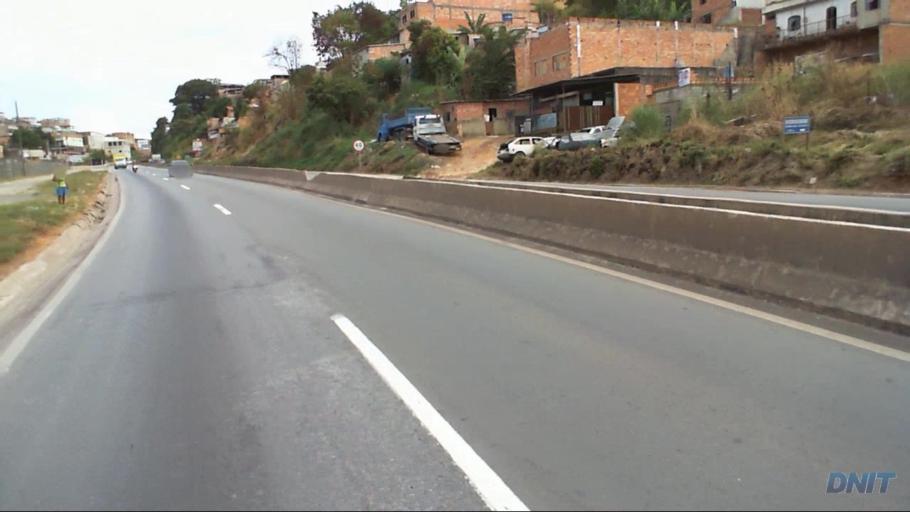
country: BR
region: Minas Gerais
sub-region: Santa Luzia
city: Santa Luzia
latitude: -19.8478
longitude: -43.8877
